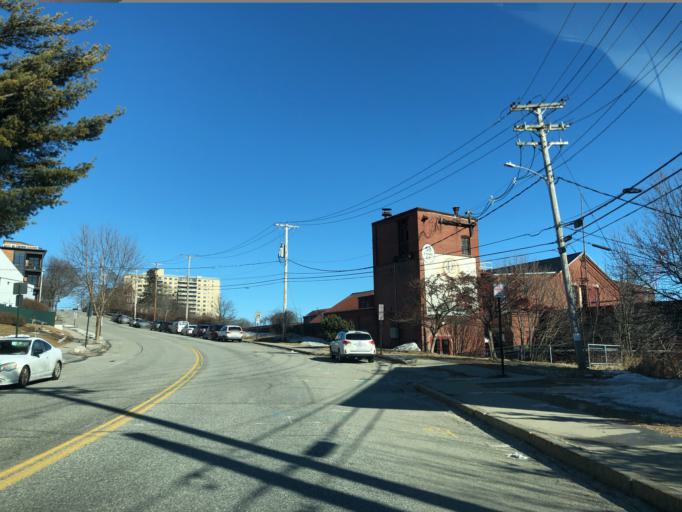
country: US
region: Maine
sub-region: Cumberland County
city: Portland
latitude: 43.6624
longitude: -70.2454
